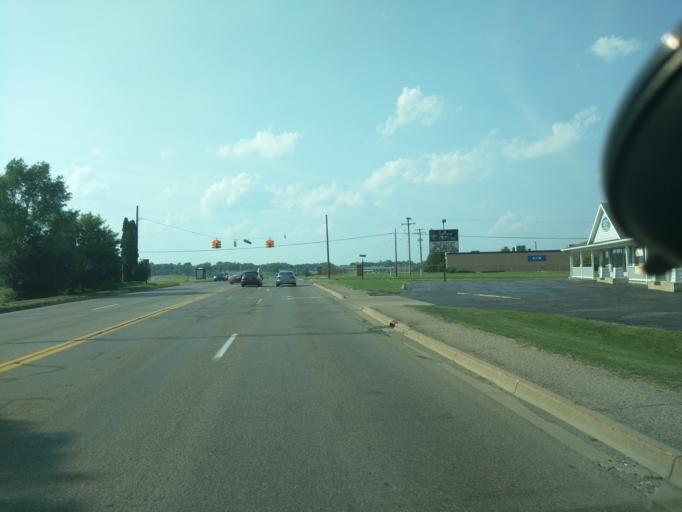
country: US
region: Michigan
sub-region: Jackson County
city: Jackson
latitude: 42.2613
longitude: -84.4480
